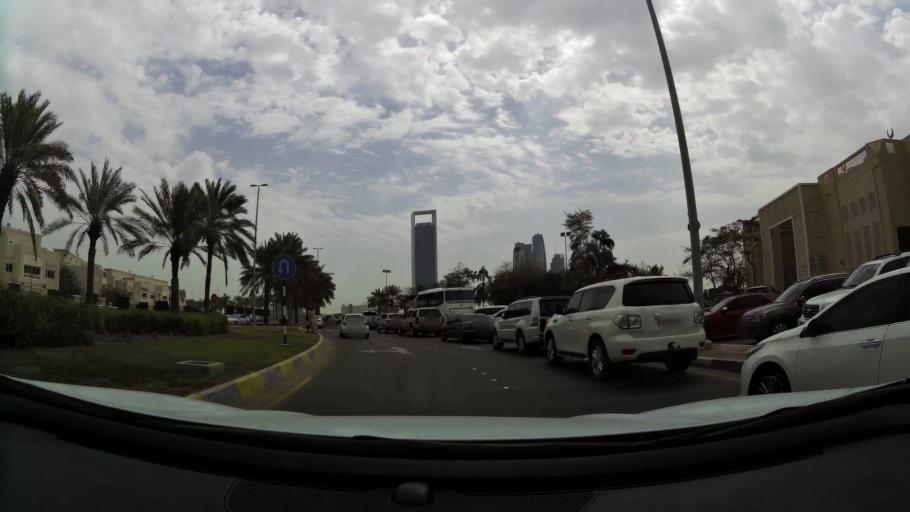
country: AE
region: Abu Dhabi
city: Abu Dhabi
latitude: 24.4730
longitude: 54.3170
